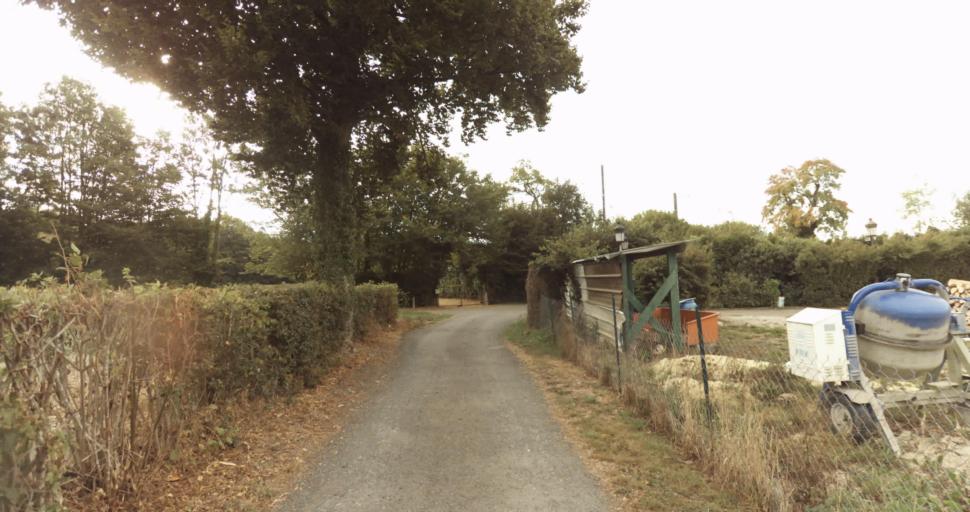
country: FR
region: Lower Normandy
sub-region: Departement de l'Orne
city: Vimoutiers
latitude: 48.9507
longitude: 0.2566
